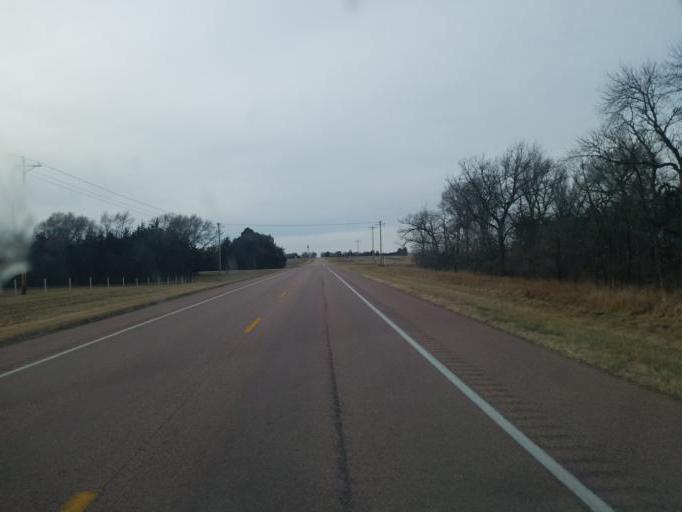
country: US
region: Nebraska
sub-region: Antelope County
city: Neligh
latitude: 42.3352
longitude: -98.1052
